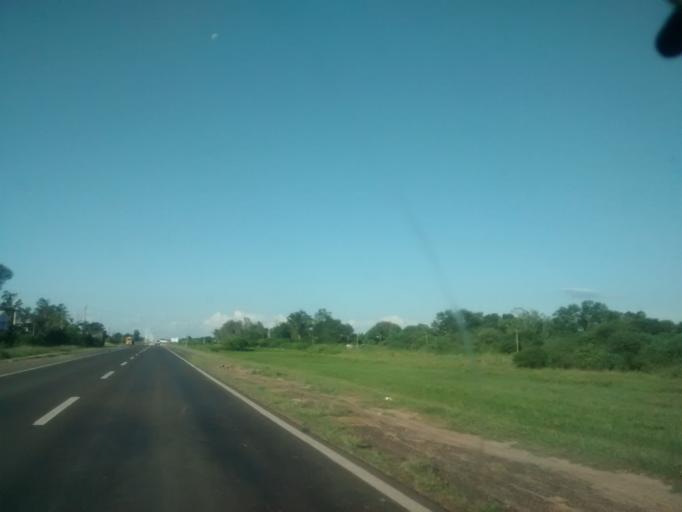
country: AR
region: Chaco
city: Fontana
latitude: -27.4712
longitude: -59.0514
